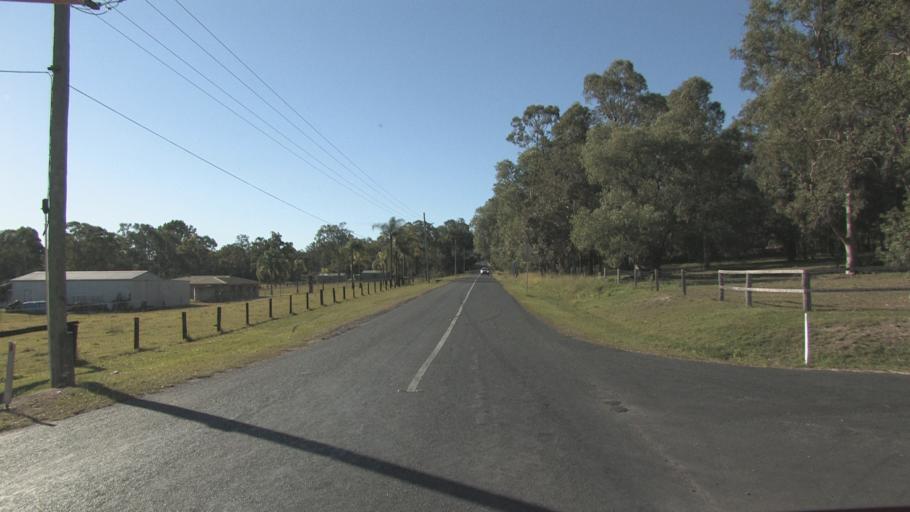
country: AU
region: Queensland
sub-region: Logan
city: Logan Reserve
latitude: -27.7355
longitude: 153.1036
